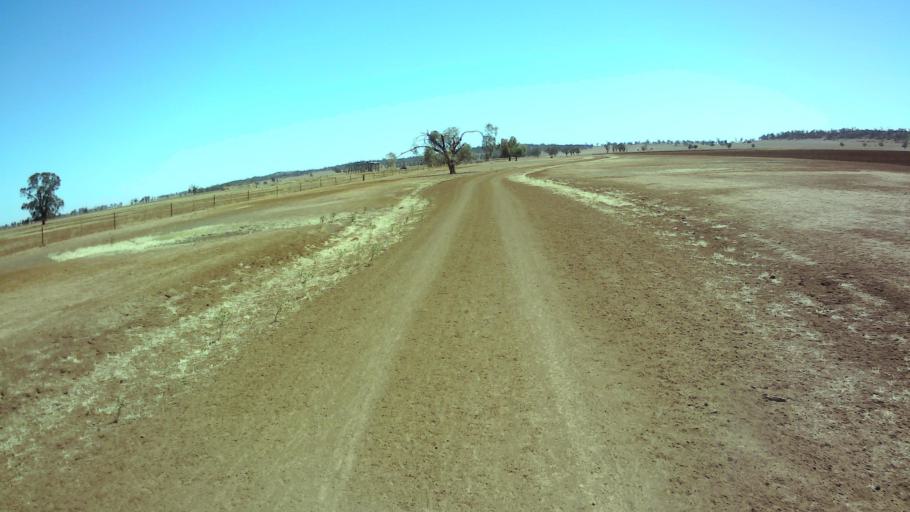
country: AU
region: New South Wales
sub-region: Forbes
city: Forbes
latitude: -33.7086
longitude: 147.6679
